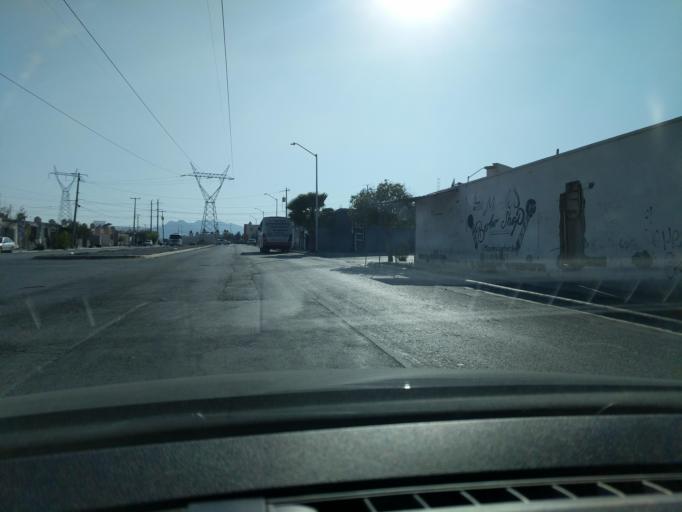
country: MX
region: Coahuila
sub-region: Ramos Arizpe
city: Ramos Arizpe
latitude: 25.5442
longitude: -100.9690
